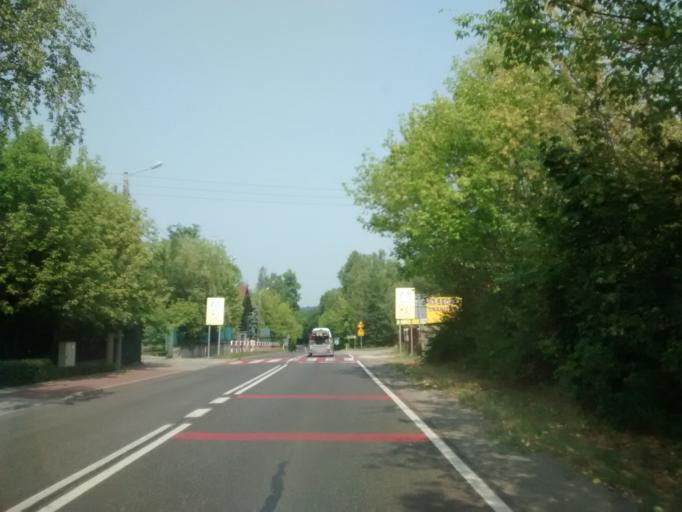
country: PL
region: Lesser Poland Voivodeship
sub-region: Powiat olkuski
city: Klucze
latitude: 50.3521
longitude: 19.5626
